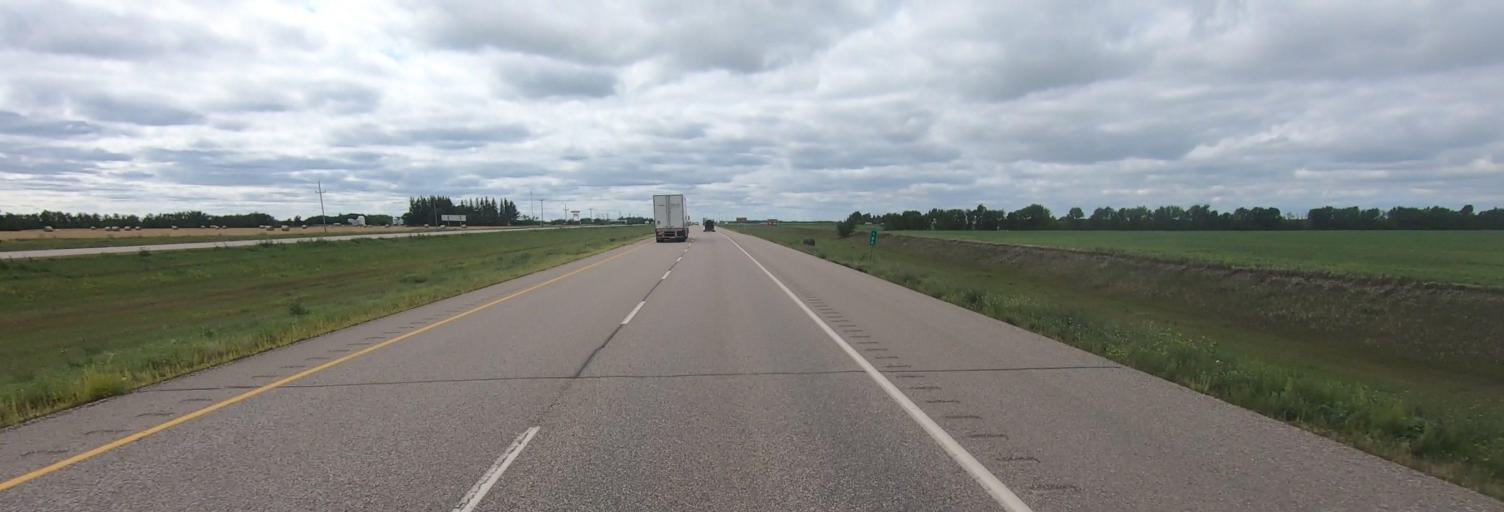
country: CA
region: Manitoba
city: Carberry
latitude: 49.9018
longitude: -99.3473
